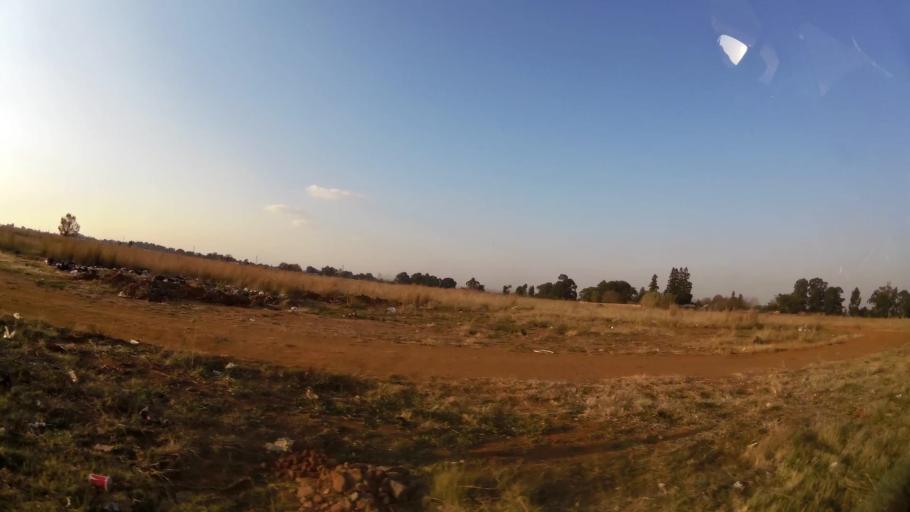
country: ZA
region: Gauteng
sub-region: Ekurhuleni Metropolitan Municipality
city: Benoni
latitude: -26.1398
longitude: 28.3835
